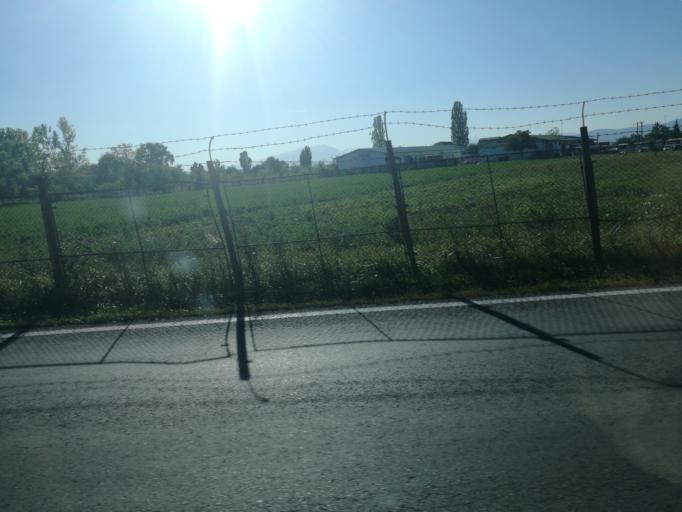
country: RO
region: Brasov
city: Brasov
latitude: 45.6819
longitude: 25.5848
